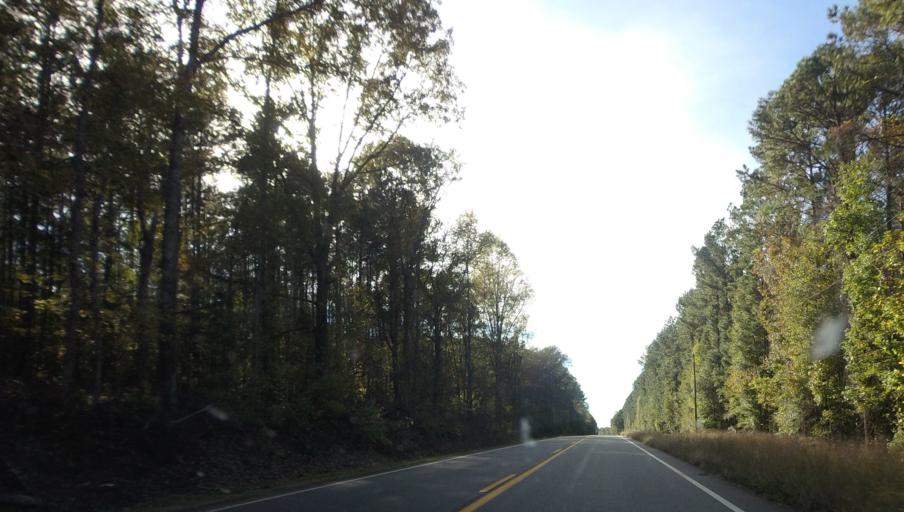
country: US
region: Georgia
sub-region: Taylor County
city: Butler
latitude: 32.7166
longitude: -84.2655
